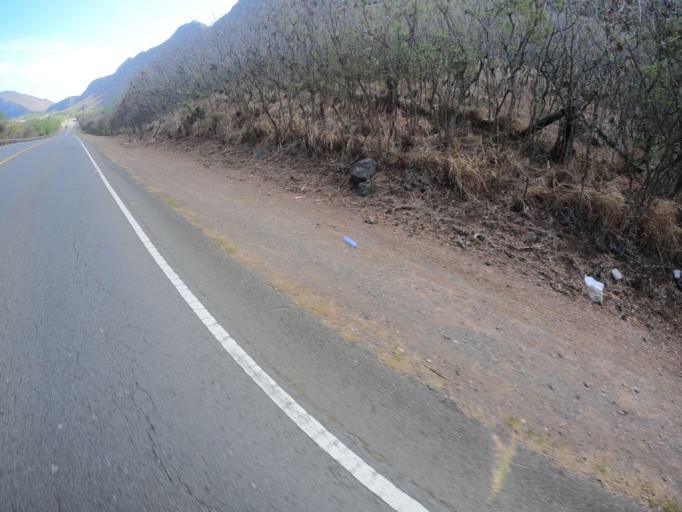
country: US
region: Hawaii
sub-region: Honolulu County
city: Waimanalo Beach
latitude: 21.3208
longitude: -157.6736
